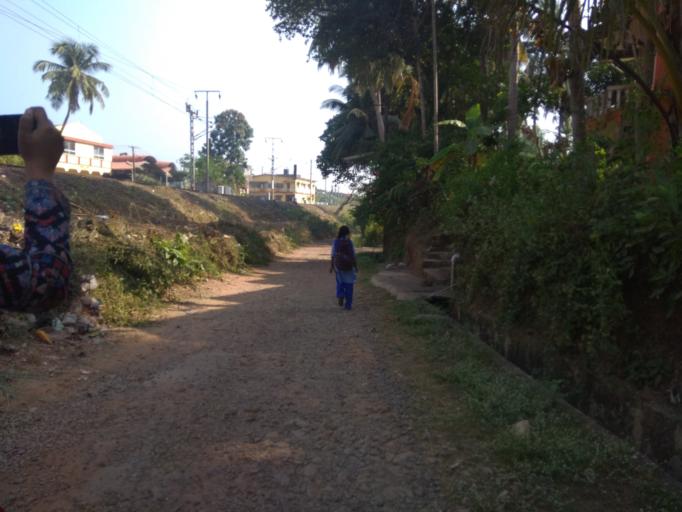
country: IN
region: Karnataka
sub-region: Dakshina Kannada
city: Ullal
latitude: 12.8467
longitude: 74.8555
